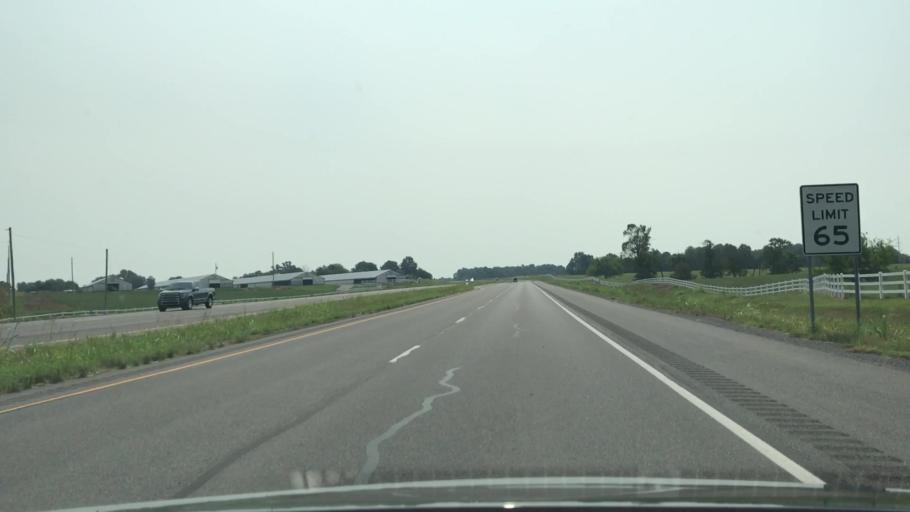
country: US
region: Kentucky
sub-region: Graves County
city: Mayfield
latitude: 36.6812
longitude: -88.5324
